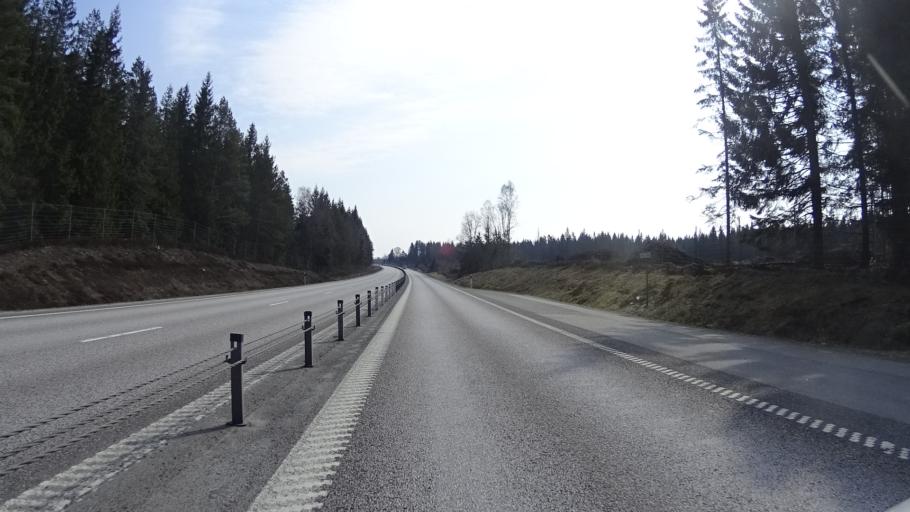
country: SE
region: Vaestra Goetaland
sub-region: Ulricehamns Kommun
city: Ulricehamn
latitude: 57.7836
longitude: 13.6482
